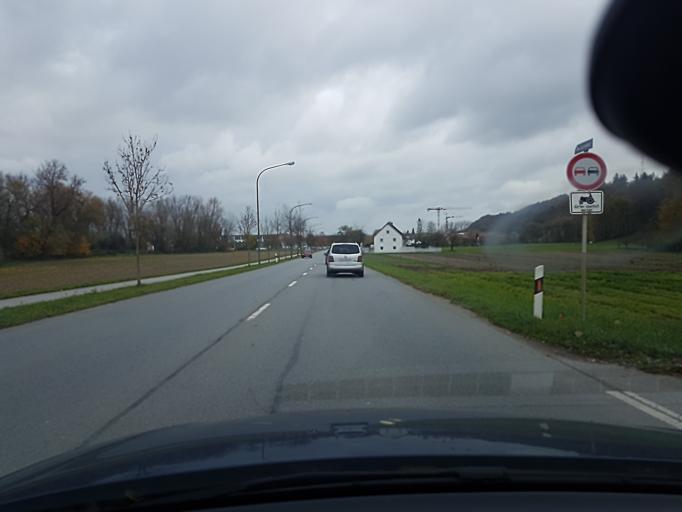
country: DE
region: Bavaria
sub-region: Lower Bavaria
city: Ergolding
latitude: 48.5514
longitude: 12.1949
